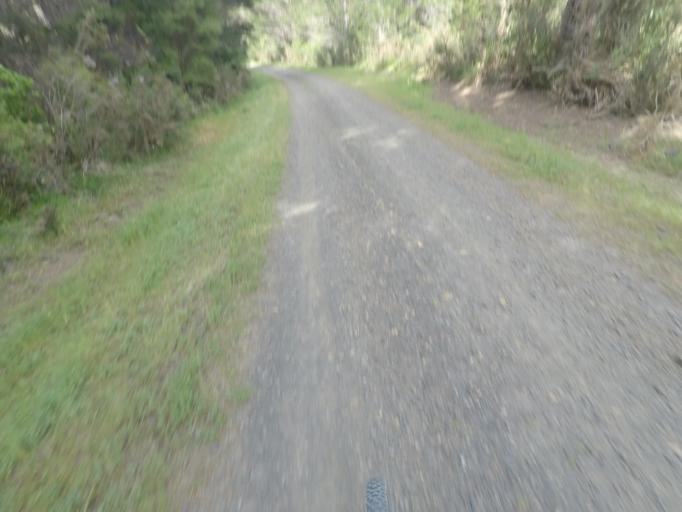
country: NZ
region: Auckland
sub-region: Auckland
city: Muriwai Beach
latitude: -36.7442
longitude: 174.5661
